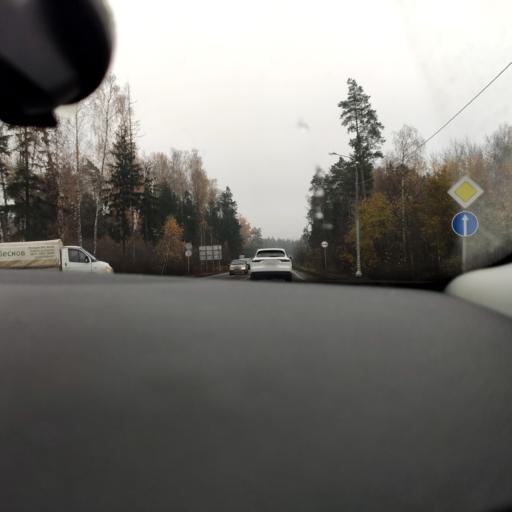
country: RU
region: Moskovskaya
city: Petrovo-Dal'neye
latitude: 55.7840
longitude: 37.1596
